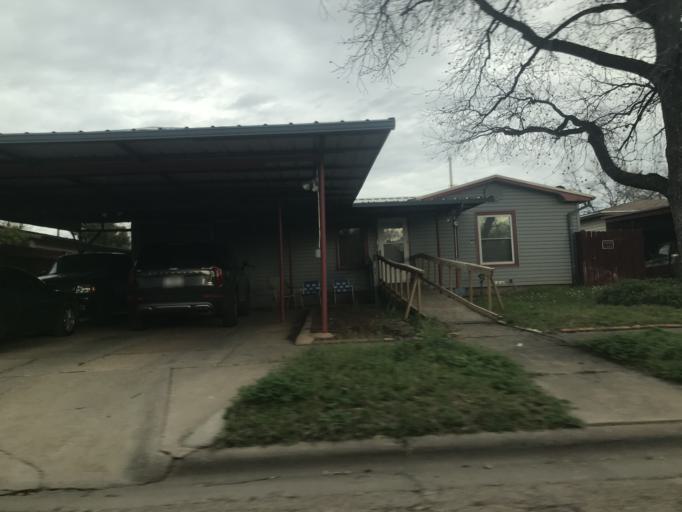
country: US
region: Texas
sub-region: Taylor County
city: Abilene
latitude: 32.4622
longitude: -99.7557
